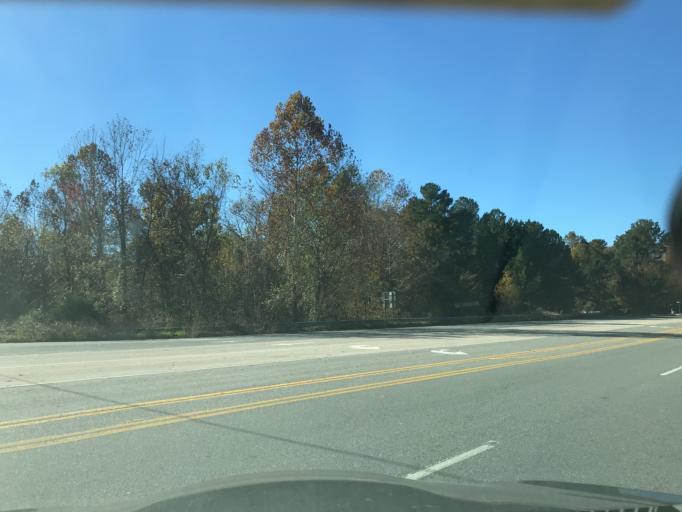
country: US
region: North Carolina
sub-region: Wake County
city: Morrisville
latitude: 35.8998
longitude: -78.7871
